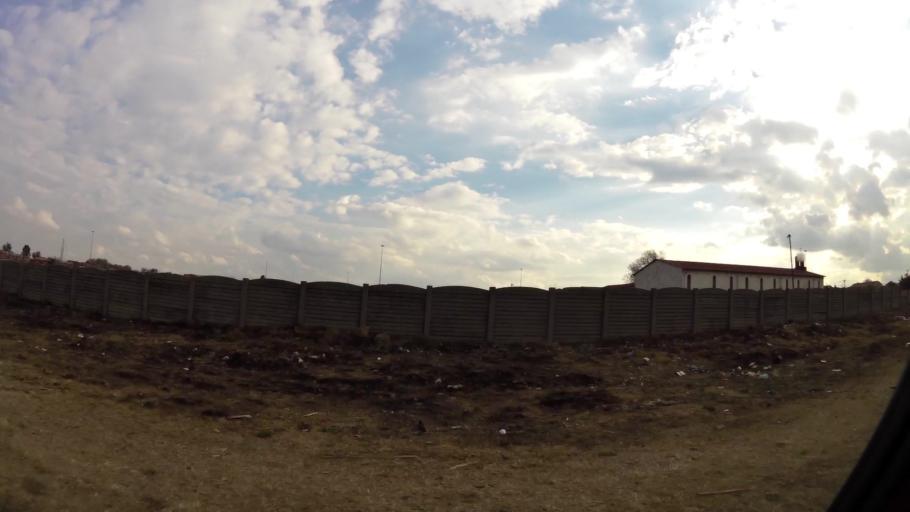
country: ZA
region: Gauteng
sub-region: Sedibeng District Municipality
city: Vereeniging
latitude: -26.6863
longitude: 27.8796
